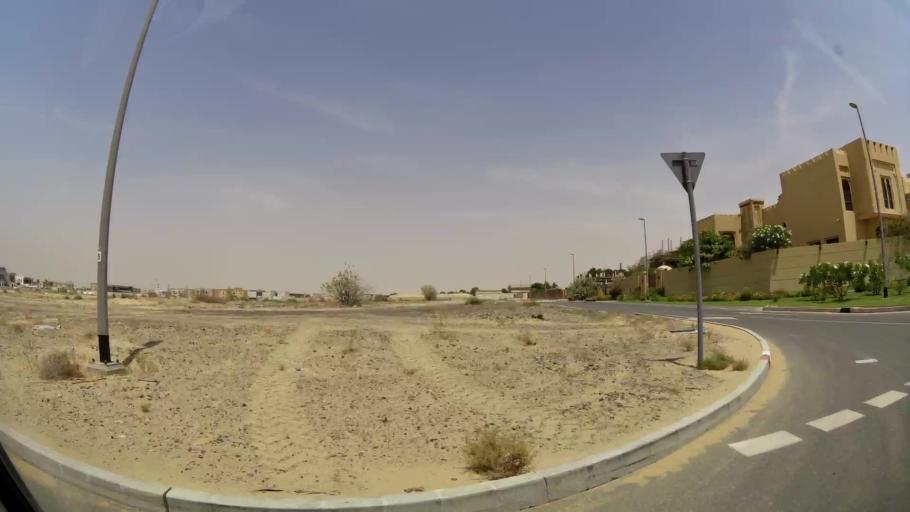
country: AE
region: Ash Shariqah
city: Sharjah
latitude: 25.2406
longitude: 55.4876
